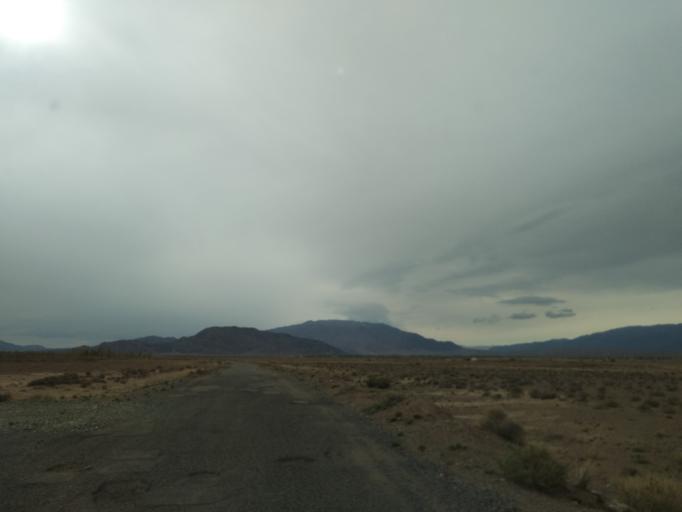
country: KG
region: Ysyk-Koel
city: Balykchy
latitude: 42.3203
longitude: 76.2236
